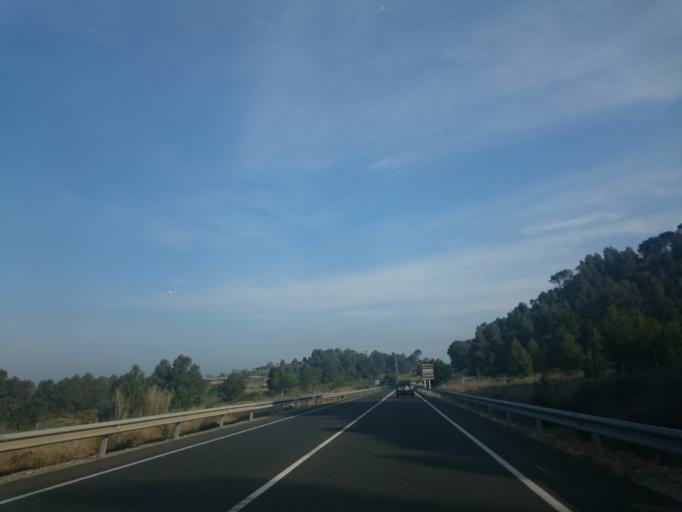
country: ES
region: Catalonia
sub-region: Provincia de Barcelona
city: La Pobla de Claramunt
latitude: 41.5704
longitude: 1.6744
